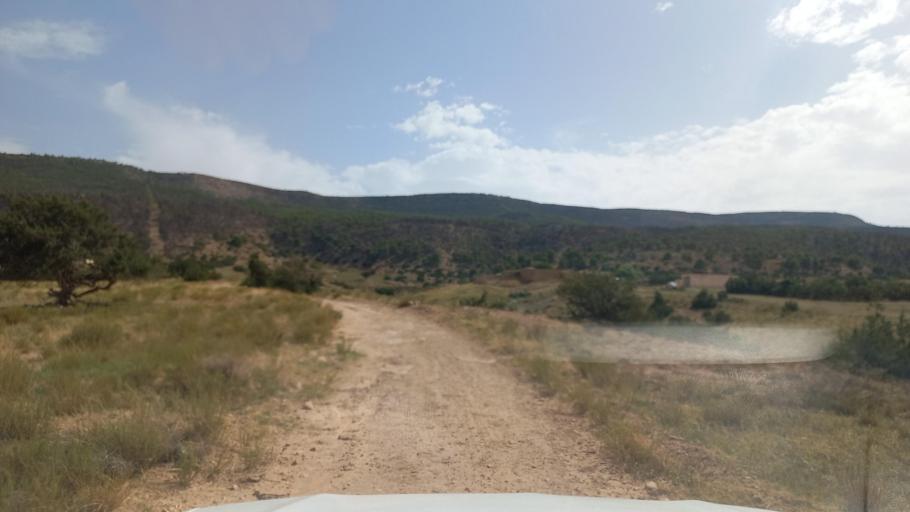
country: TN
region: Al Qasrayn
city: Kasserine
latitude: 35.3569
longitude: 8.8887
